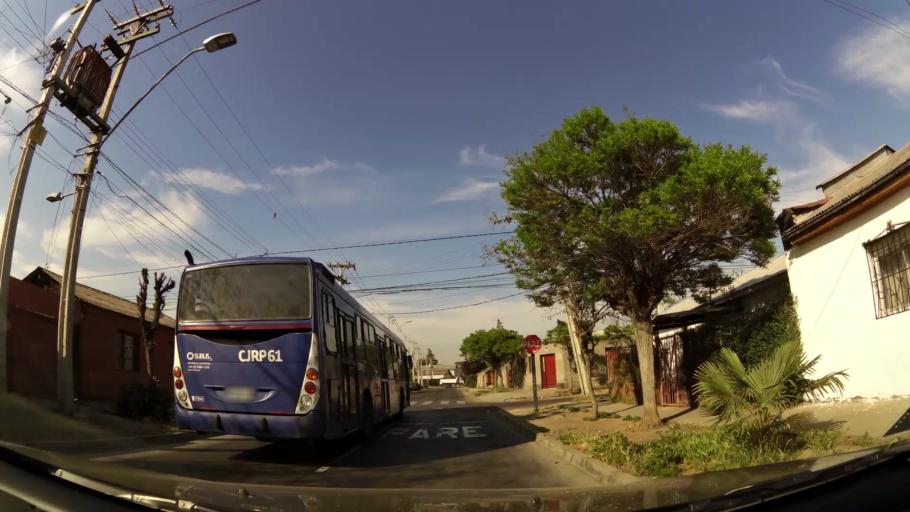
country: CL
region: Santiago Metropolitan
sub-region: Provincia de Maipo
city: San Bernardo
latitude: -33.6069
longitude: -70.7046
